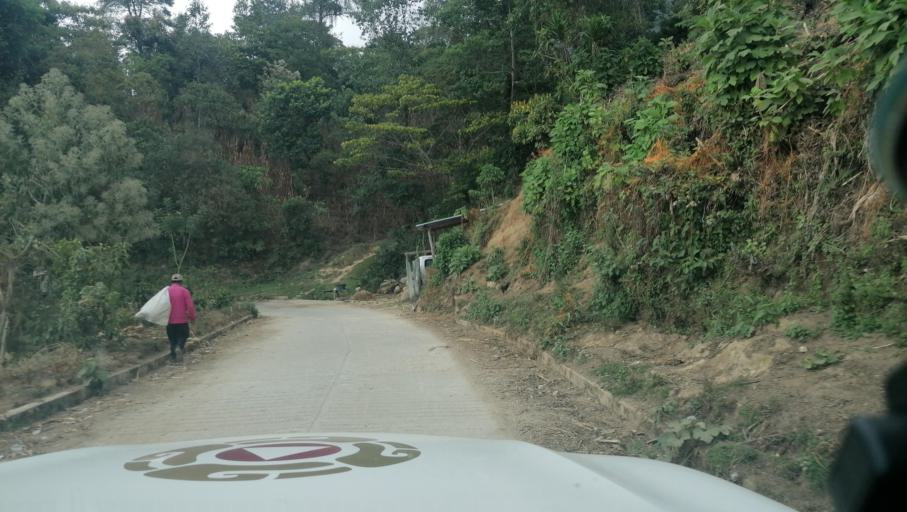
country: GT
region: San Marcos
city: Tacana
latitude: 15.2004
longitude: -92.1789
